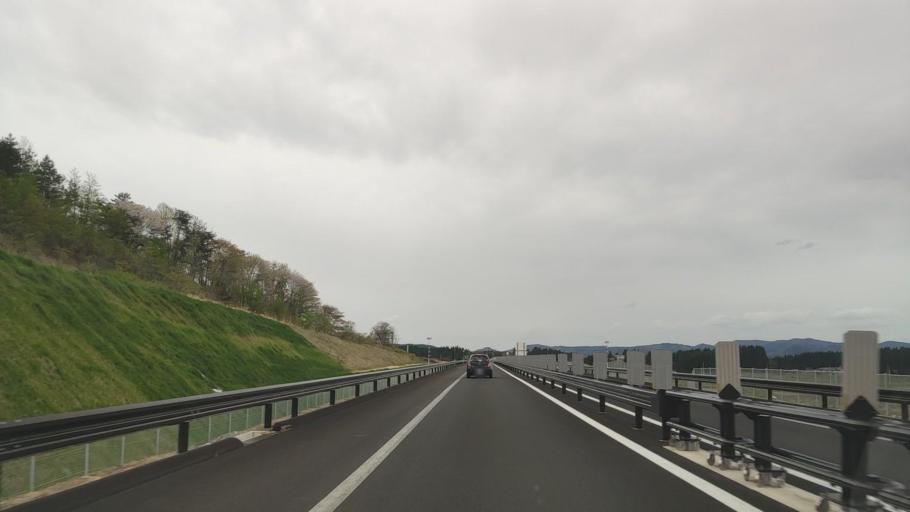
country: JP
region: Akita
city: Takanosu
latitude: 40.1996
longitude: 140.3626
